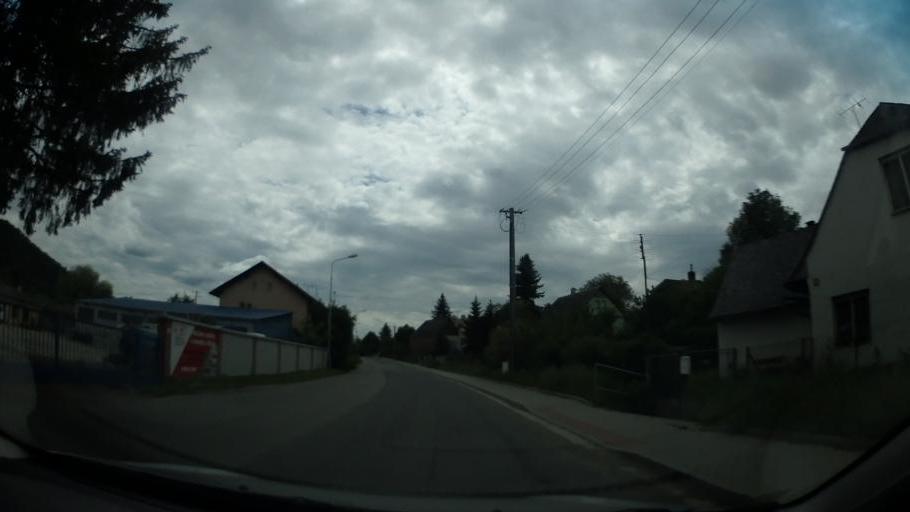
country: CZ
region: Pardubicky
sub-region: Okres Svitavy
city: Moravska Trebova
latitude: 49.7718
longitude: 16.6634
